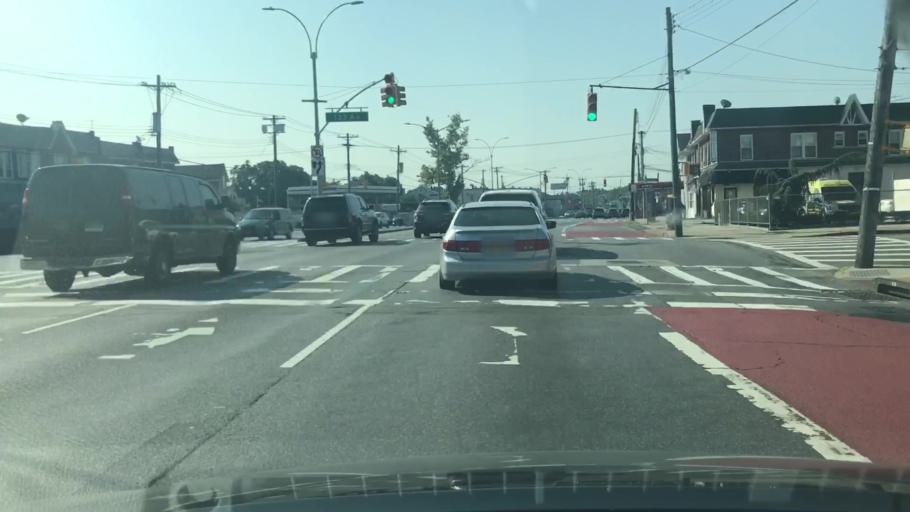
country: US
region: New York
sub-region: Queens County
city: Borough of Queens
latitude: 40.6755
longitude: -73.8435
